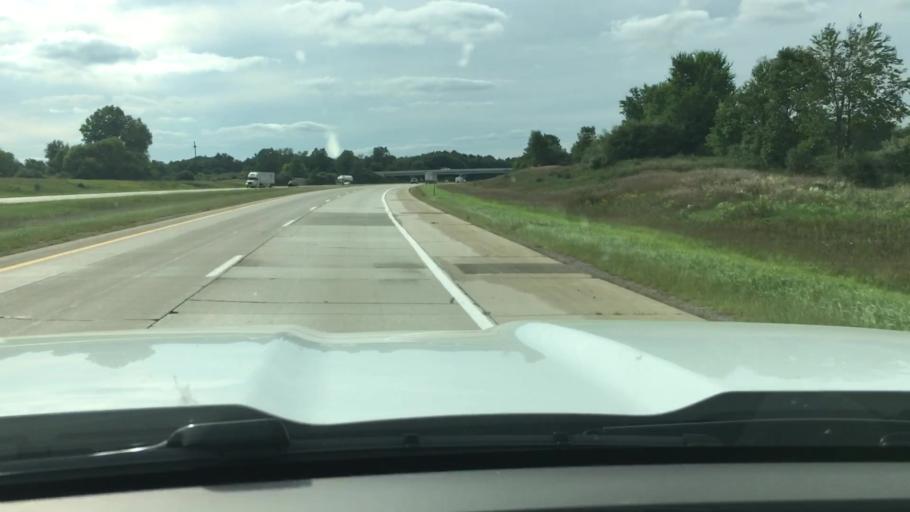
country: US
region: Michigan
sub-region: Lapeer County
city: Lapeer
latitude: 43.0120
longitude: -83.2758
